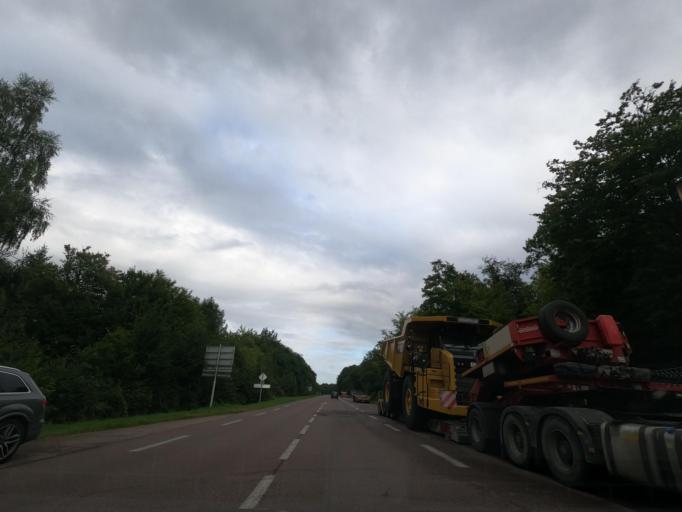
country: FR
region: Haute-Normandie
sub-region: Departement de la Seine-Maritime
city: Sahurs
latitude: 49.3430
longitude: 0.9363
